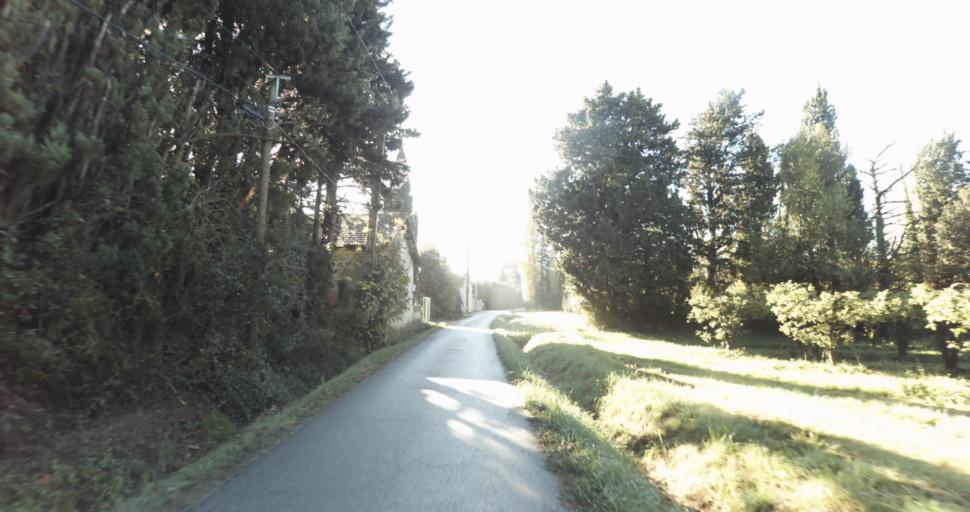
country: FR
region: Provence-Alpes-Cote d'Azur
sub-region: Departement des Bouches-du-Rhone
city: Rognonas
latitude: 43.8845
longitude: 4.8035
